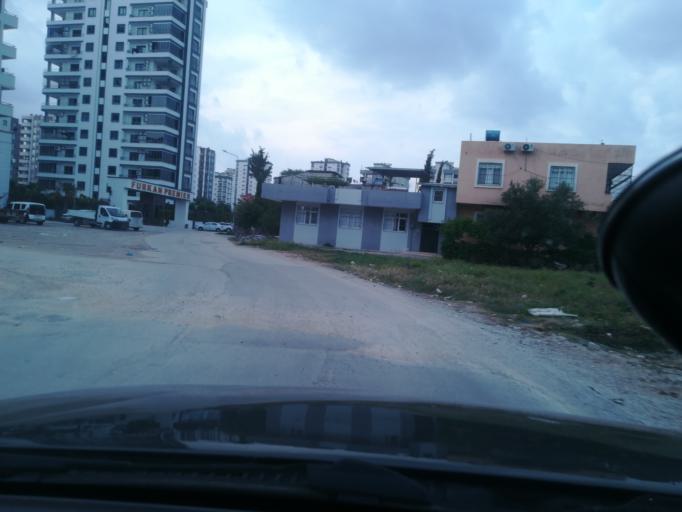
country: TR
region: Adana
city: Seyhan
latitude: 37.0117
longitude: 35.2716
